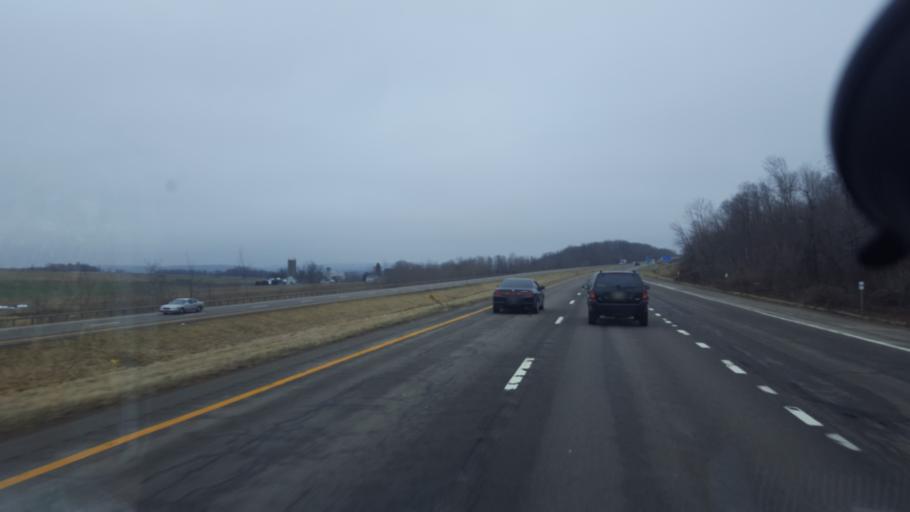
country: US
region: New York
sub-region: Cattaraugus County
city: Randolph
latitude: 42.1618
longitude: -79.0279
